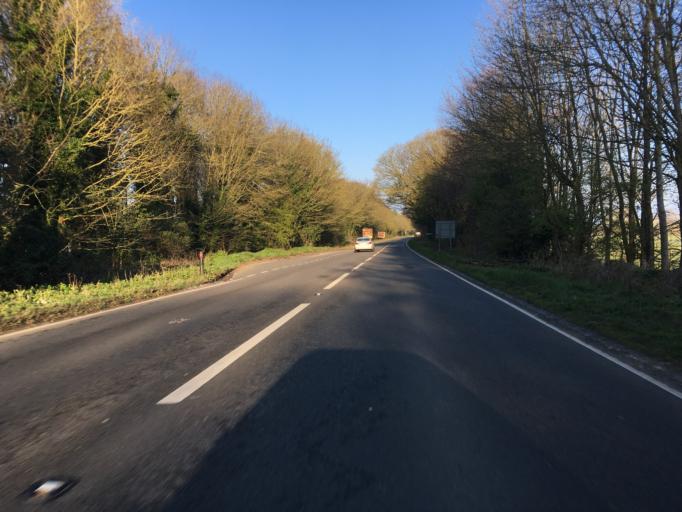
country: GB
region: England
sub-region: Gloucestershire
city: Northleach
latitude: 51.8259
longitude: -1.7995
